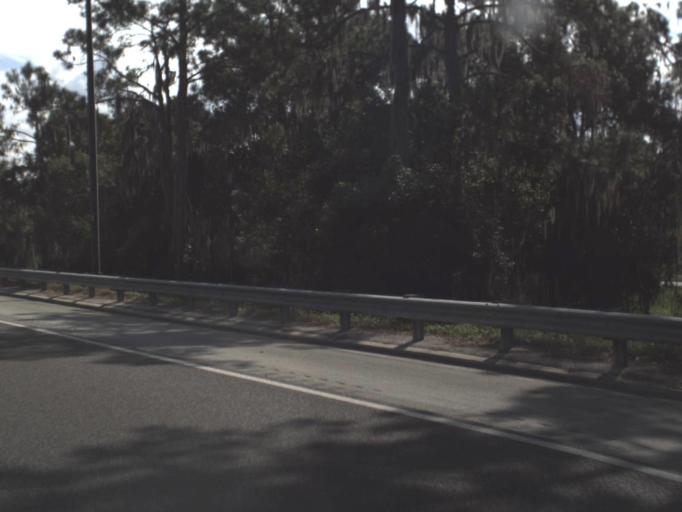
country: US
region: Florida
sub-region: Polk County
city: Medulla
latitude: 27.9963
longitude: -81.9674
